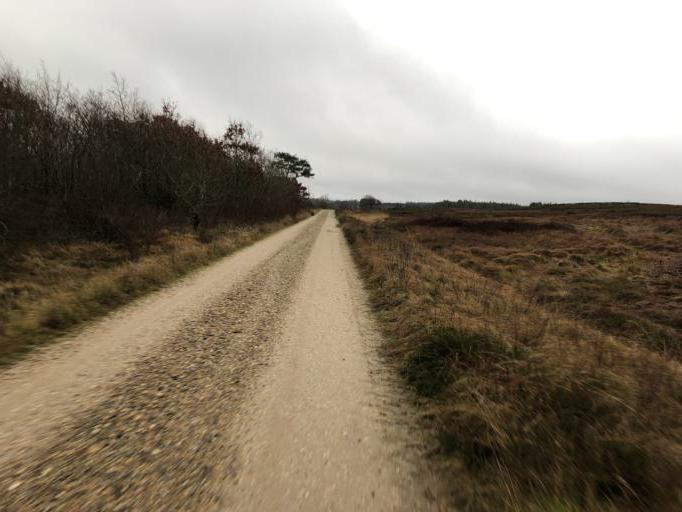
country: DK
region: Central Jutland
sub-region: Holstebro Kommune
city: Ulfborg
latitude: 56.2859
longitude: 8.4611
